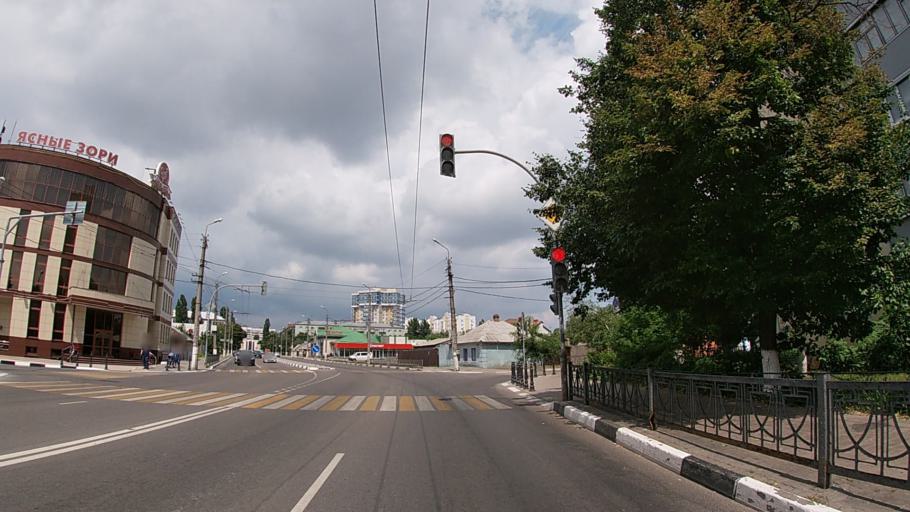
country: RU
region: Belgorod
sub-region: Belgorodskiy Rayon
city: Belgorod
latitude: 50.6091
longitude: 36.5920
